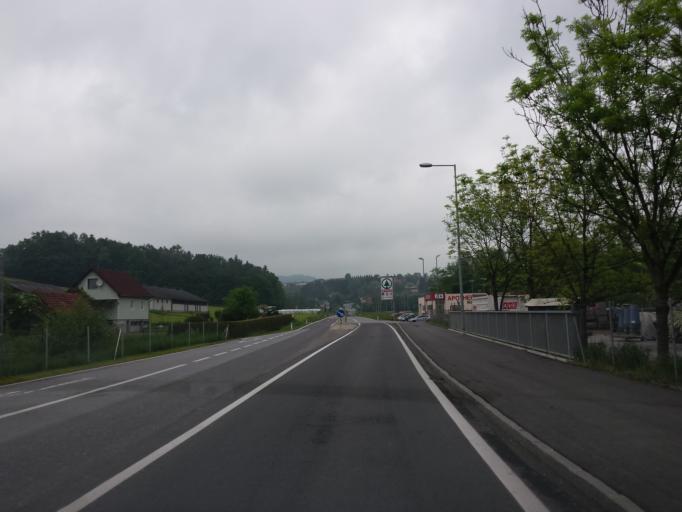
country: AT
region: Styria
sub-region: Politischer Bezirk Graz-Umgebung
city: Kumberg
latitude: 47.1445
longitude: 15.5486
